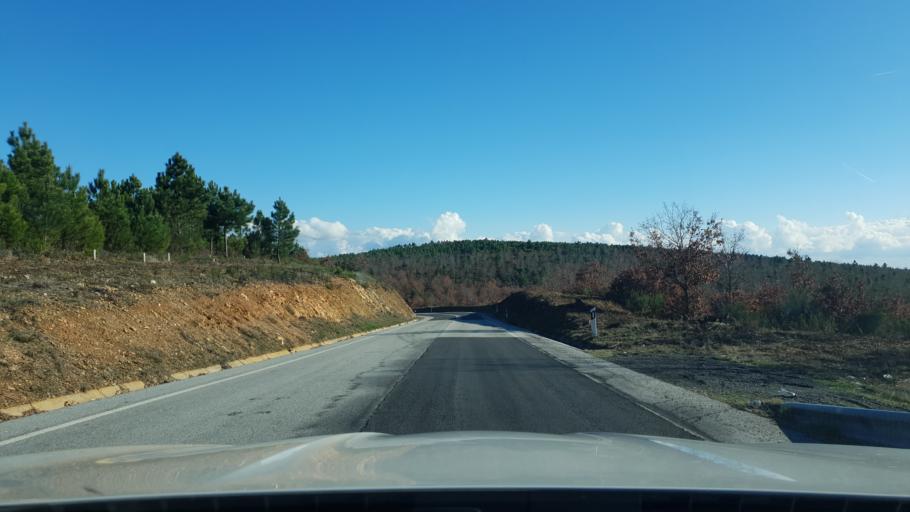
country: PT
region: Braganca
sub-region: Freixo de Espada A Cinta
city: Freixo de Espada a Cinta
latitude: 41.1395
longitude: -6.8071
